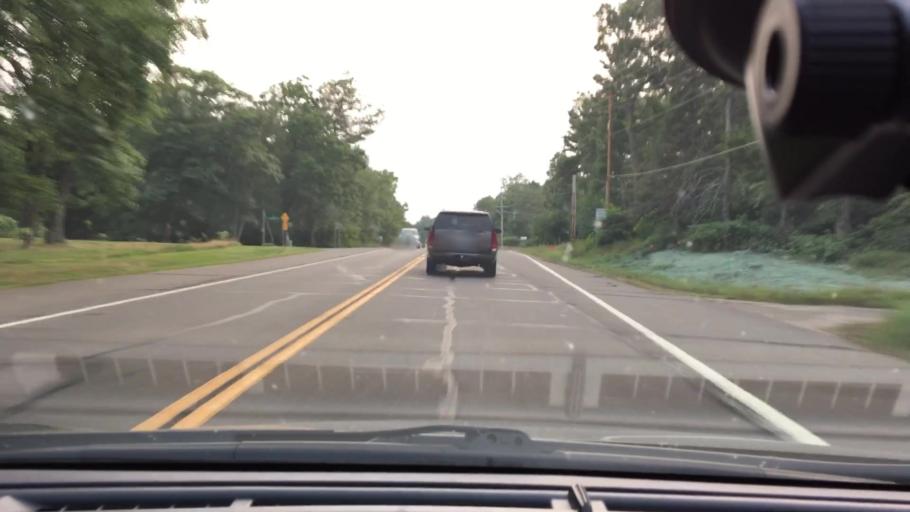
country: US
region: Minnesota
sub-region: Crow Wing County
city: Crosby
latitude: 46.4905
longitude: -93.9259
